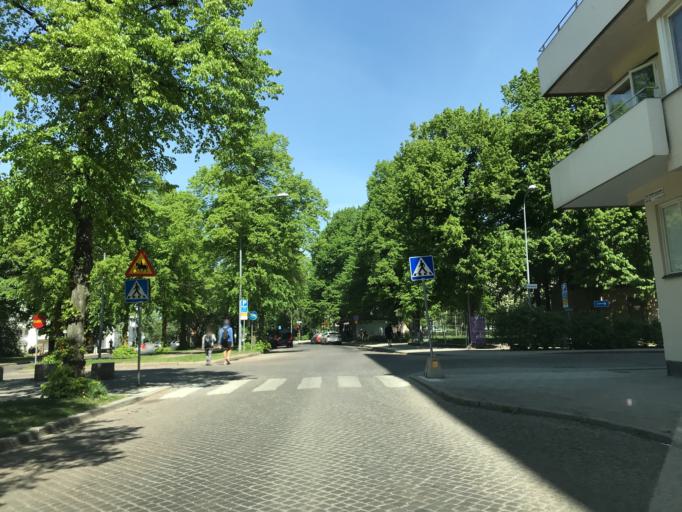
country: SE
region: Stockholm
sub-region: Stockholms Kommun
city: OEstermalm
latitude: 59.3442
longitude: 18.0931
